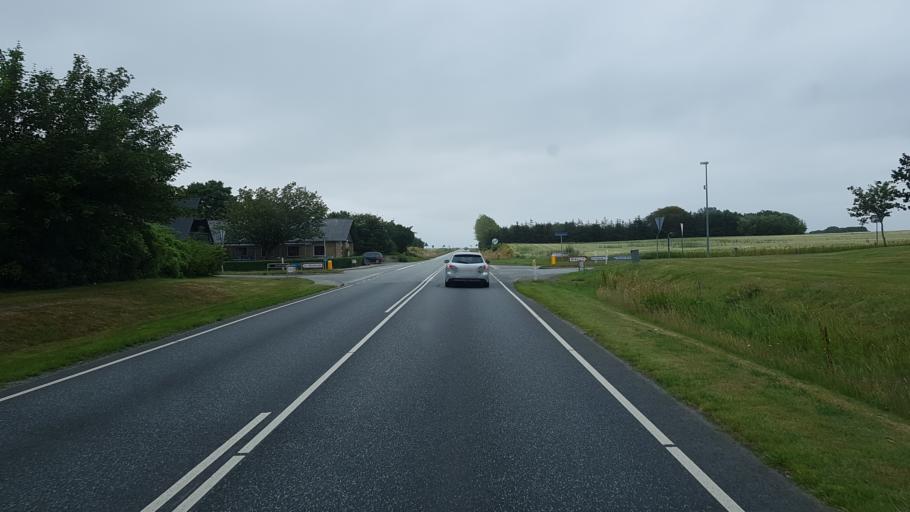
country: DK
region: Central Jutland
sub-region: Struer Kommune
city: Struer
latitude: 56.5151
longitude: 8.5362
